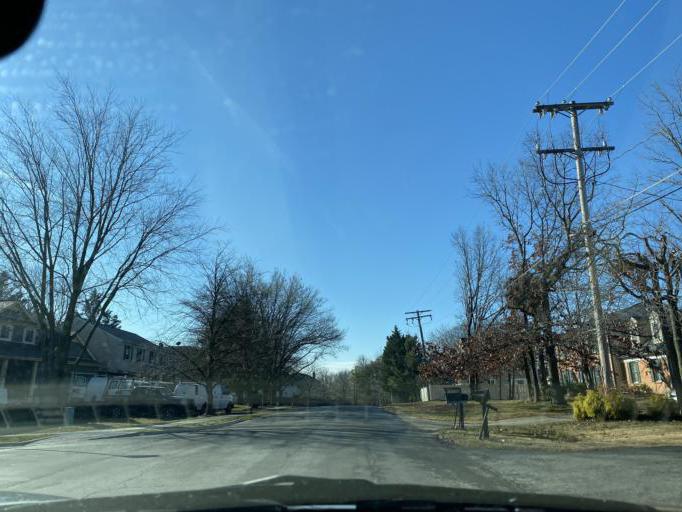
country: US
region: Maryland
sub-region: Montgomery County
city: Burtonsville
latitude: 39.1036
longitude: -76.9210
